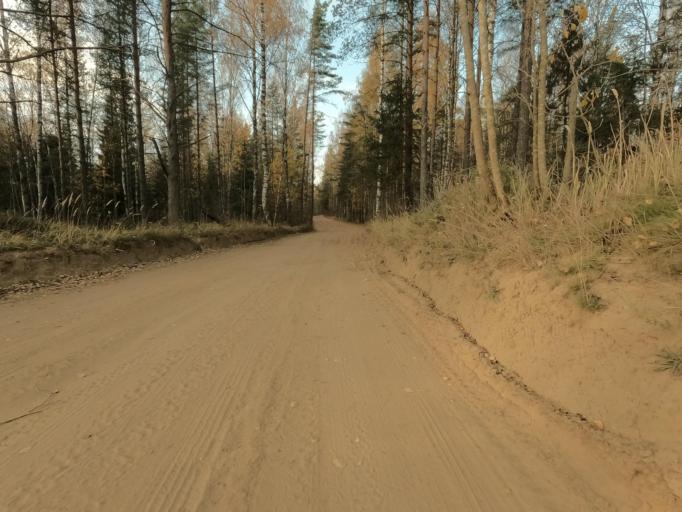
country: RU
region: Leningrad
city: Priladozhskiy
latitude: 59.7396
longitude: 31.3161
